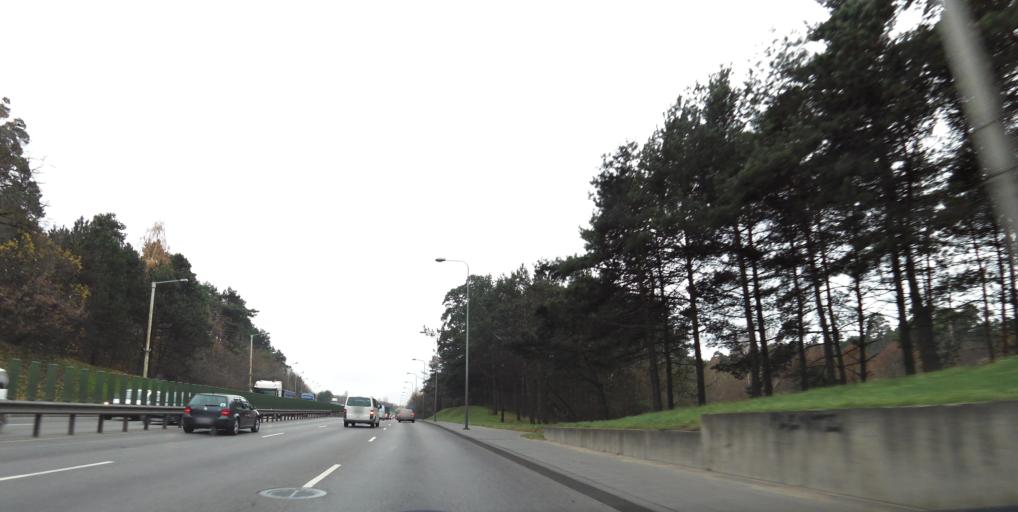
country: LT
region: Vilnius County
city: Vilkpede
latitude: 54.6814
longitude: 25.2481
